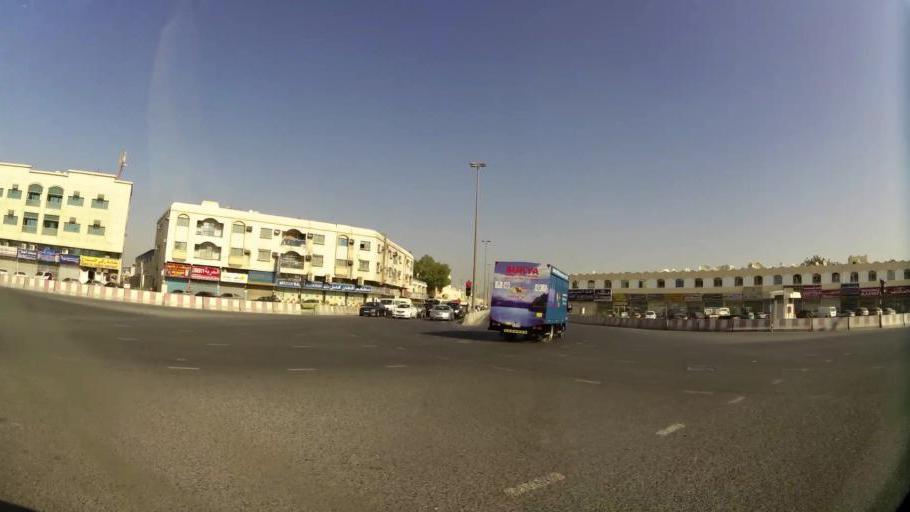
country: AE
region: Ash Shariqah
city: Sharjah
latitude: 25.3162
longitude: 55.4117
